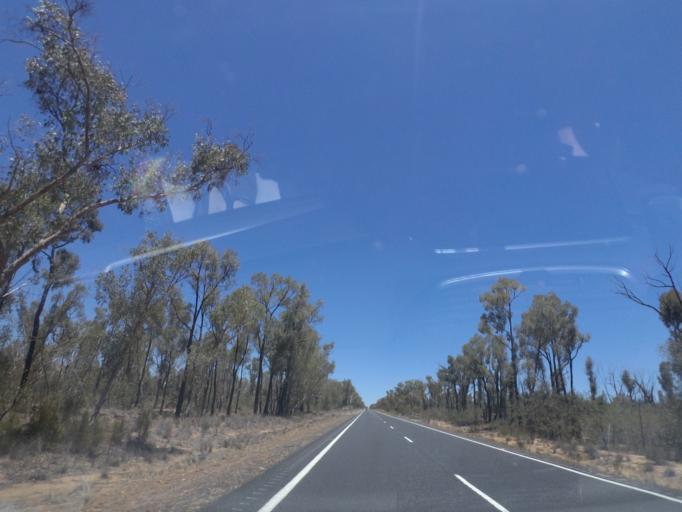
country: AU
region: New South Wales
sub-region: Warrumbungle Shire
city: Coonabarabran
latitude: -30.9471
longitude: 149.4220
